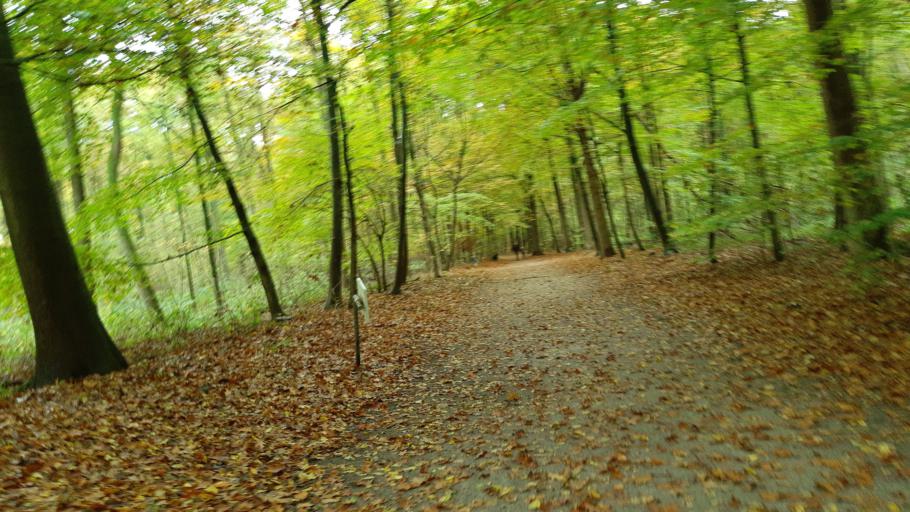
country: NL
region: Friesland
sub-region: Gemeente Lemsterland
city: Echtenerbrug
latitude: 52.7817
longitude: 5.8407
